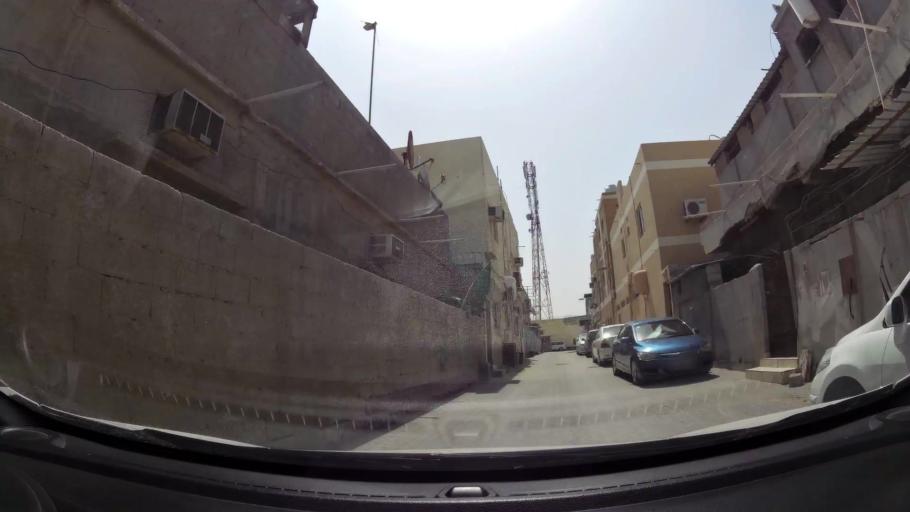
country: BH
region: Manama
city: Jidd Hafs
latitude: 26.2279
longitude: 50.4785
